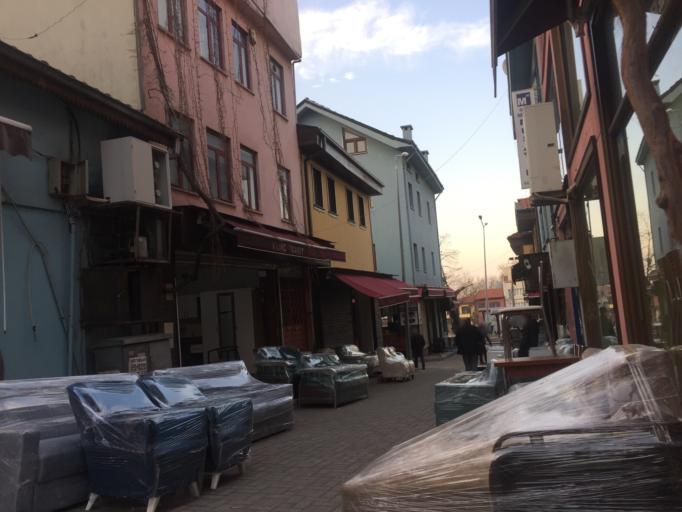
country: TR
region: Bursa
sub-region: Osmangazi
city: Bursa
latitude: 40.1840
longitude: 29.0706
